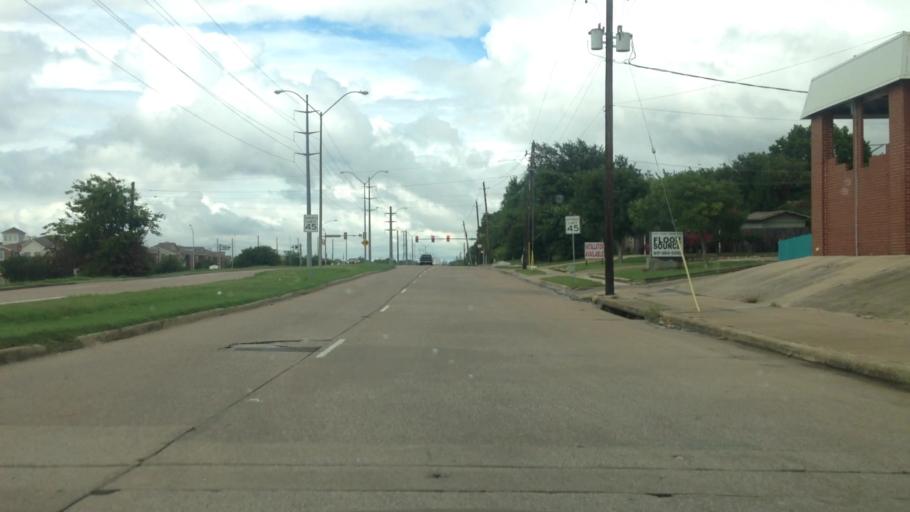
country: US
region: Texas
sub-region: Tarrant County
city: Benbrook
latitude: 32.6532
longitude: -97.4071
